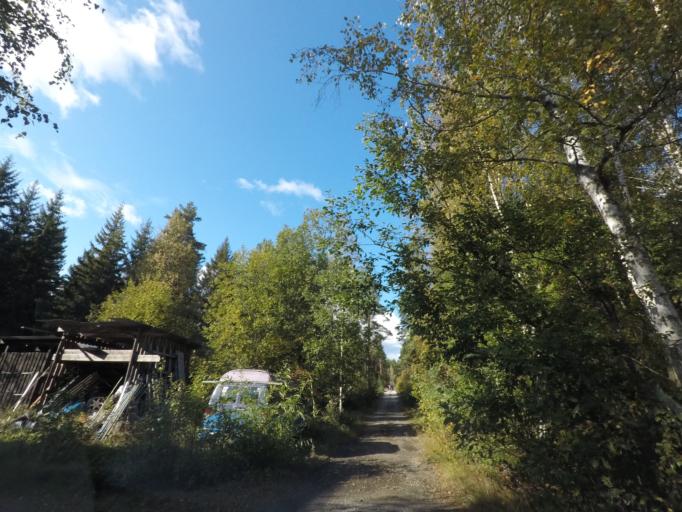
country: SE
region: Vaestmanland
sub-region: Skinnskattebergs Kommun
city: Skinnskatteberg
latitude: 59.8303
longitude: 15.5503
